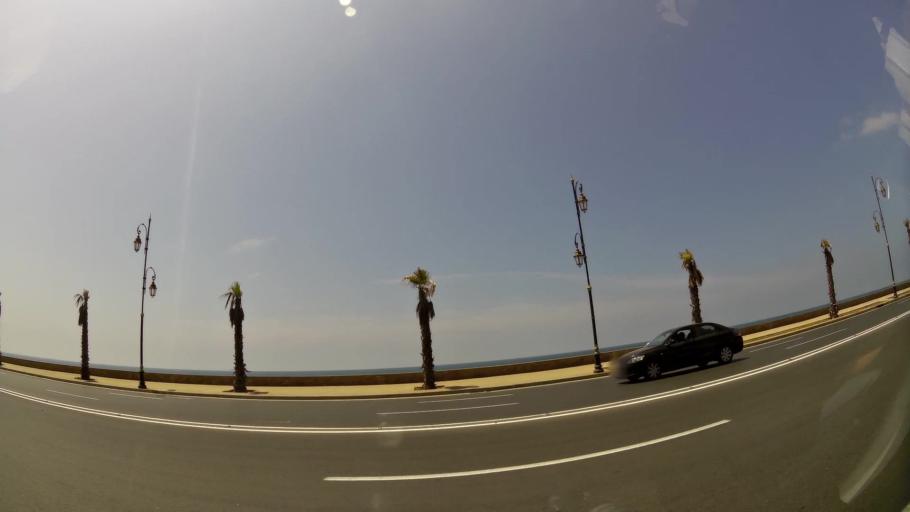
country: MA
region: Rabat-Sale-Zemmour-Zaer
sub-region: Rabat
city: Rabat
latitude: 34.0142
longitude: -6.8623
